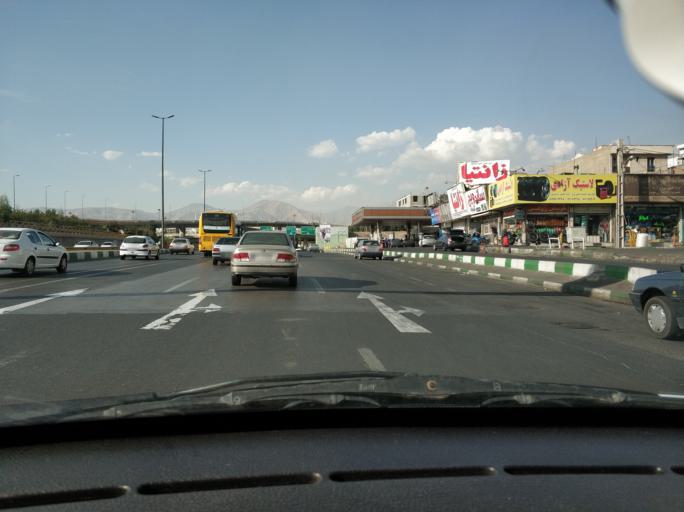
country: IR
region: Tehran
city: Tehran
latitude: 35.7091
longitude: 51.3370
